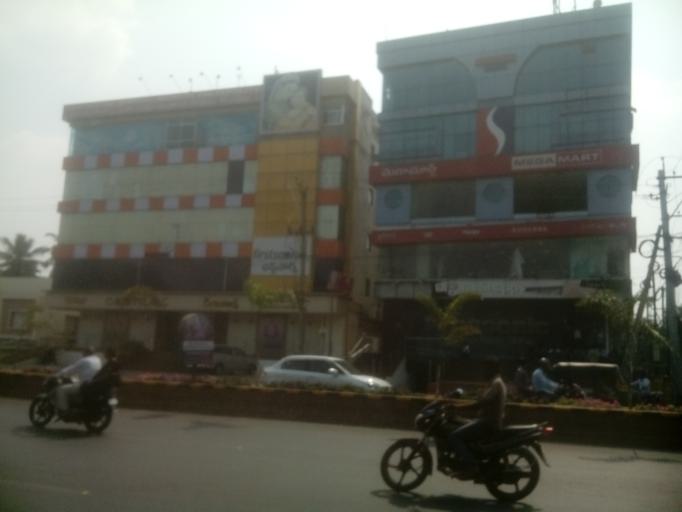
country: IN
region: Andhra Pradesh
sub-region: Krishna
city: Vijayawada
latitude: 16.5046
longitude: 80.6347
